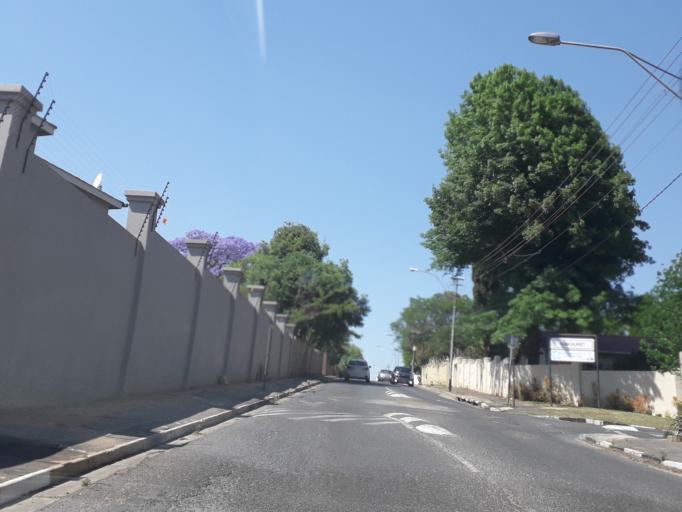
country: ZA
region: Gauteng
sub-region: City of Johannesburg Metropolitan Municipality
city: Johannesburg
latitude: -26.1341
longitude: 28.0249
